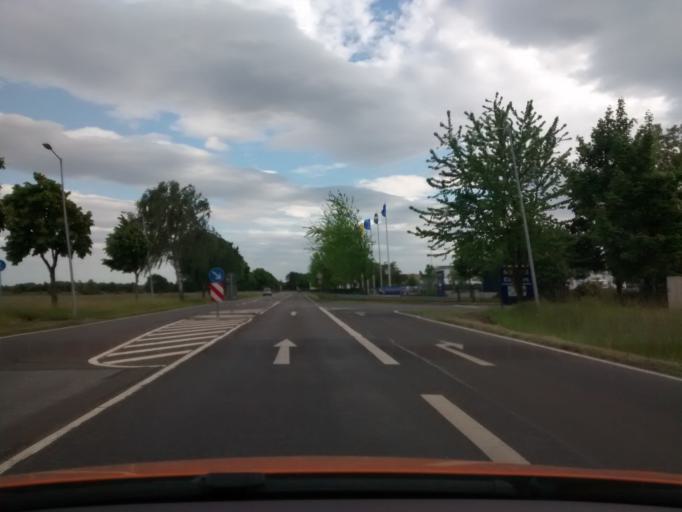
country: DE
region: Berlin
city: Bohnsdorf
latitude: 52.3765
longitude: 13.5657
